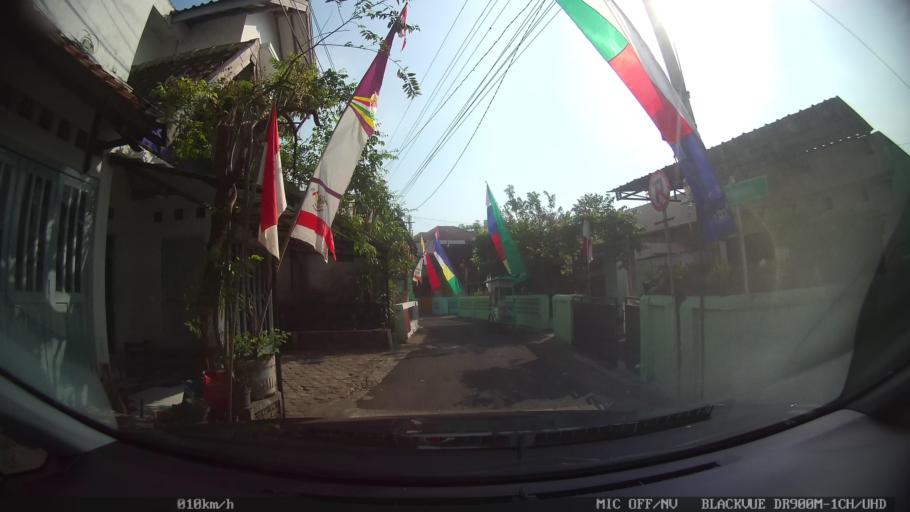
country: ID
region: Daerah Istimewa Yogyakarta
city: Yogyakarta
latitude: -7.7860
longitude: 110.3539
